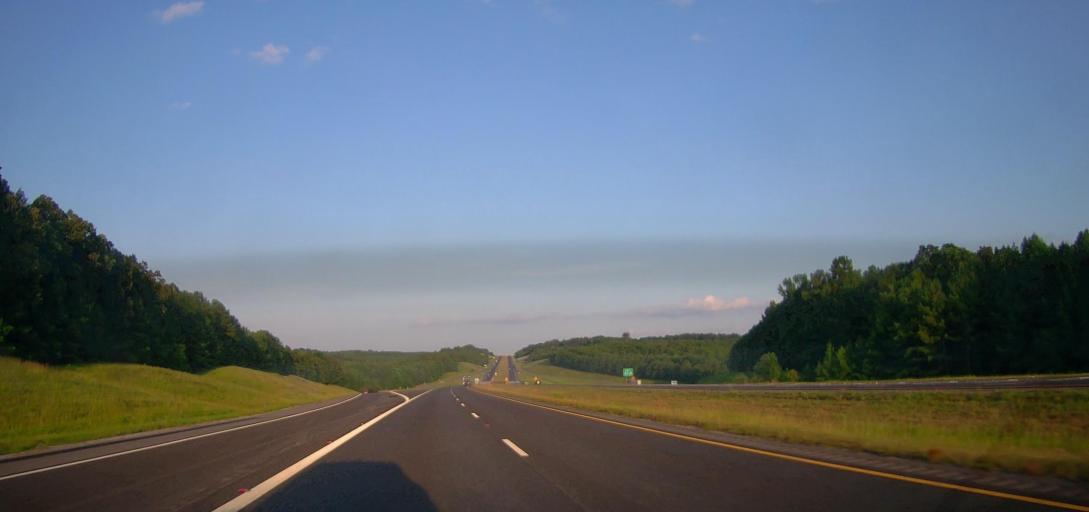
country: US
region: Alabama
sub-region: Marion County
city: Guin
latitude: 34.0434
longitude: -87.8932
